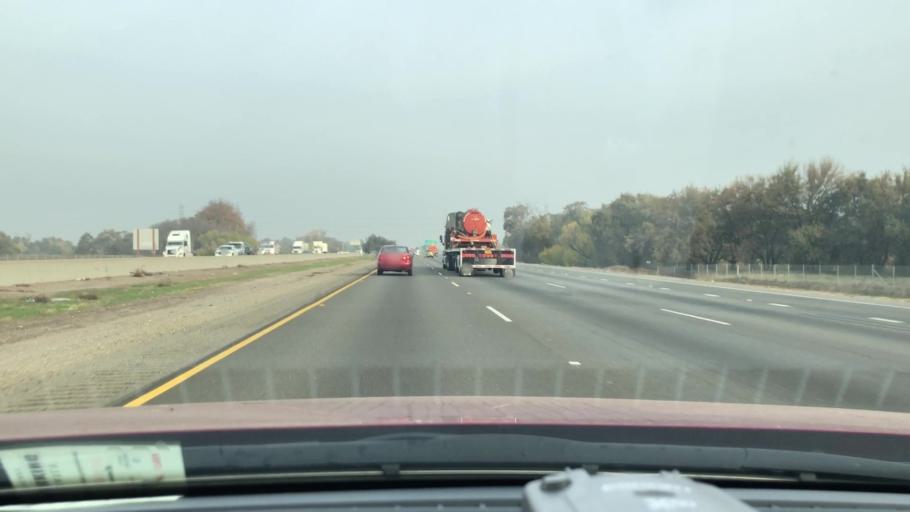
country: US
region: California
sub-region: San Joaquin County
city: Taft Mosswood
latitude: 37.9053
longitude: -121.2864
